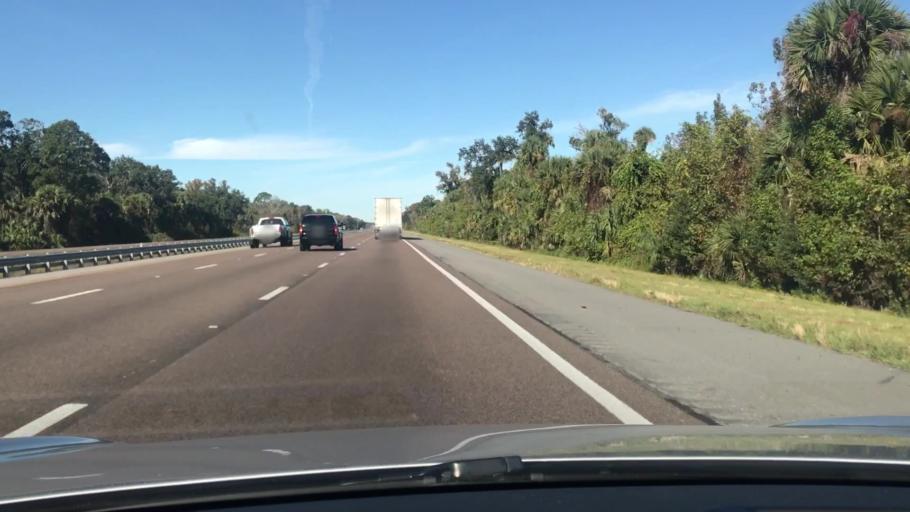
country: US
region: Florida
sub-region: Volusia County
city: Oak Hill
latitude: 28.8138
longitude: -80.9059
